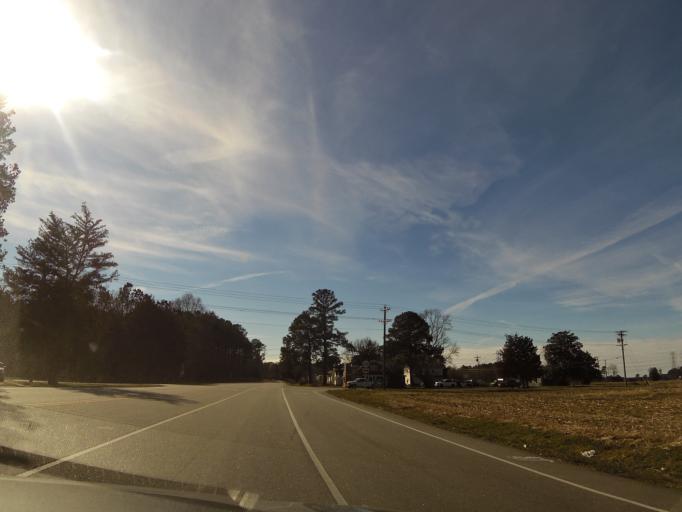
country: US
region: Virginia
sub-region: Isle of Wight County
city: Smithfield
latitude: 36.9616
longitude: -76.6640
